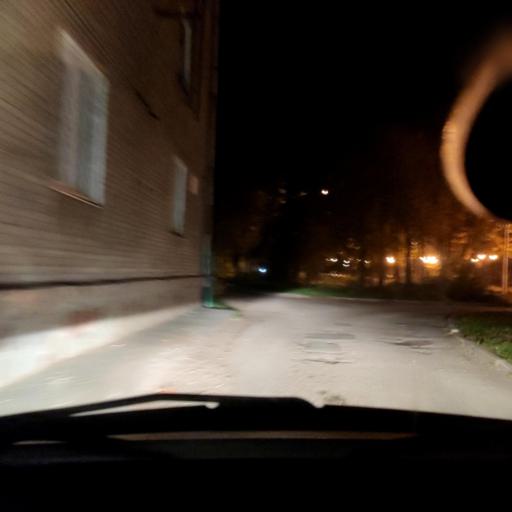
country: RU
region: Bashkortostan
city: Ufa
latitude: 54.8210
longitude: 56.0611
